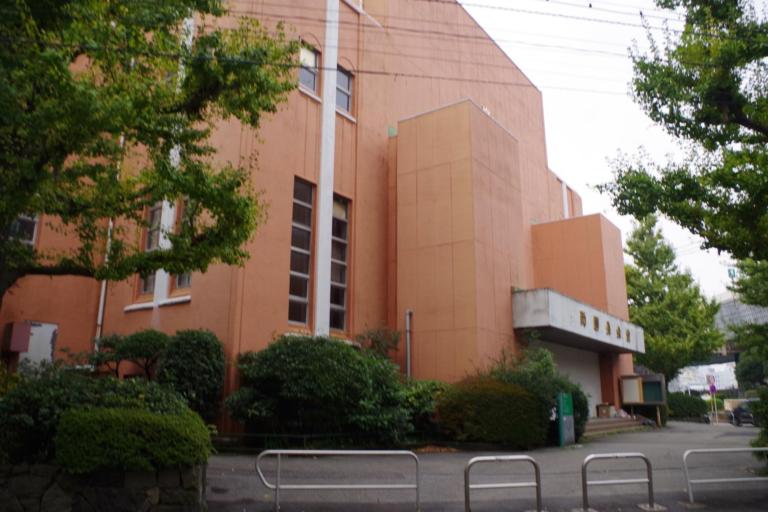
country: JP
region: Tokyo
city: Urayasu
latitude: 35.6991
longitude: 139.7937
